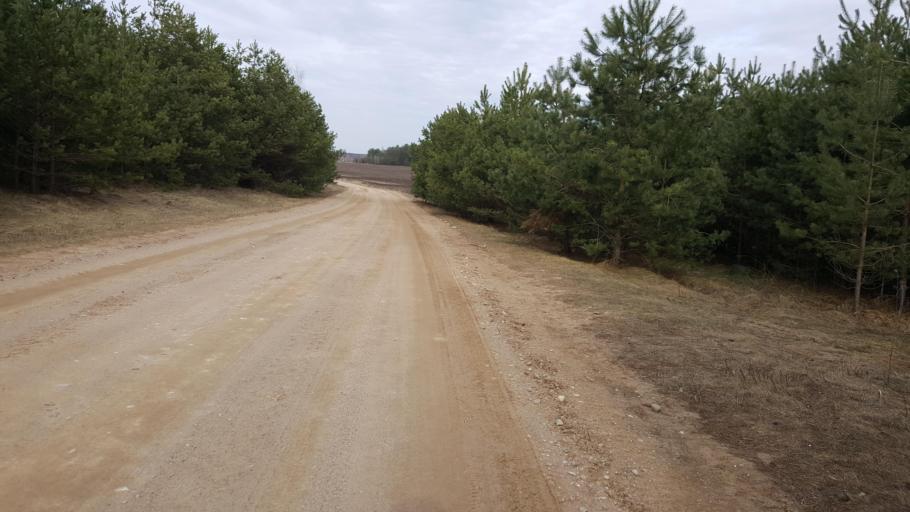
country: BY
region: Brest
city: Zhabinka
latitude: 52.3779
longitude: 23.9896
